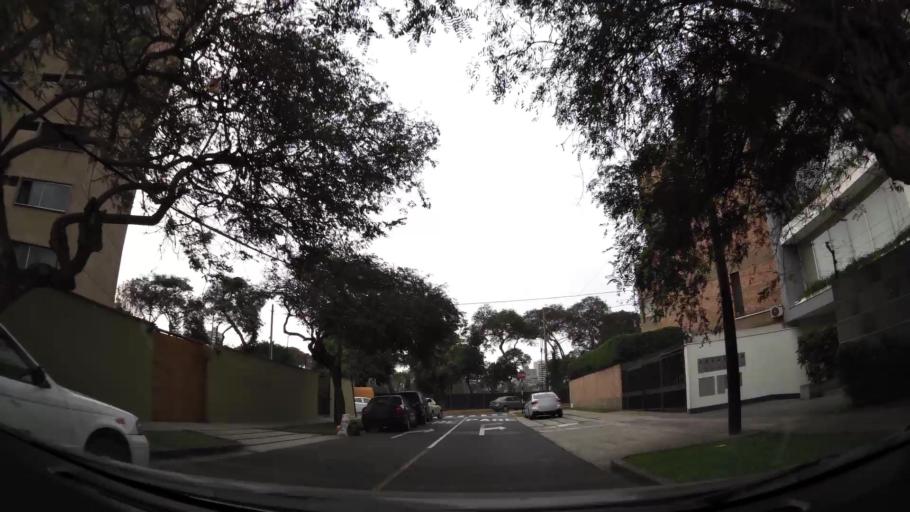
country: PE
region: Lima
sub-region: Lima
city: San Isidro
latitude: -12.1033
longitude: -77.0501
